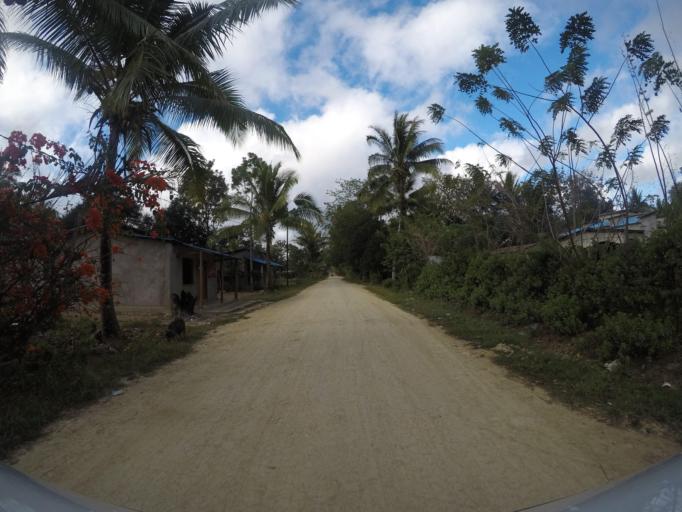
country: TL
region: Lautem
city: Lospalos
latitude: -8.5060
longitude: 126.9945
